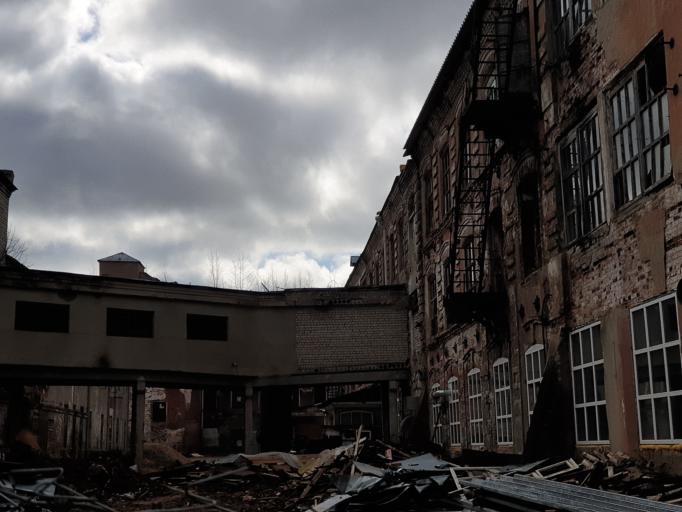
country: RU
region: Kostroma
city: Nerekhta
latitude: 57.4854
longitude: 40.6067
